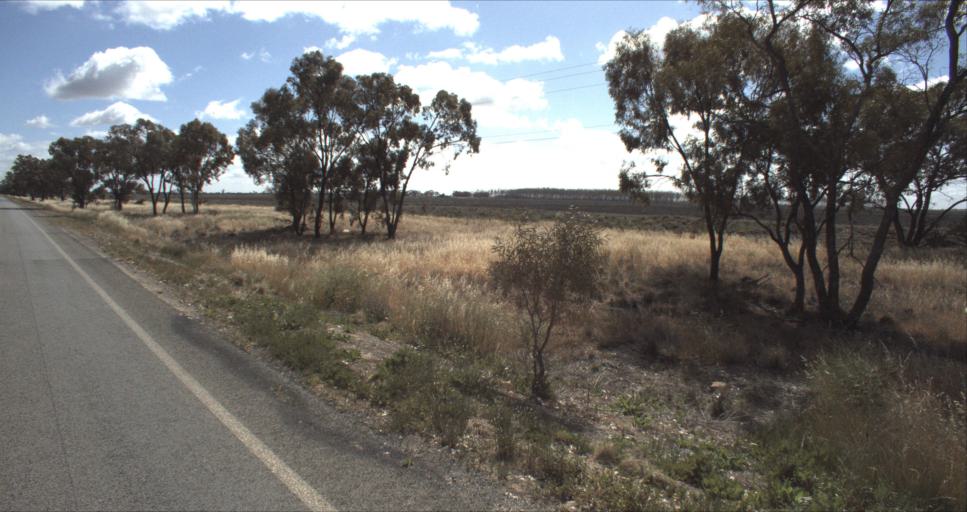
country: AU
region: New South Wales
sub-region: Murrumbidgee Shire
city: Darlington Point
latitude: -34.5665
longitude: 146.1680
